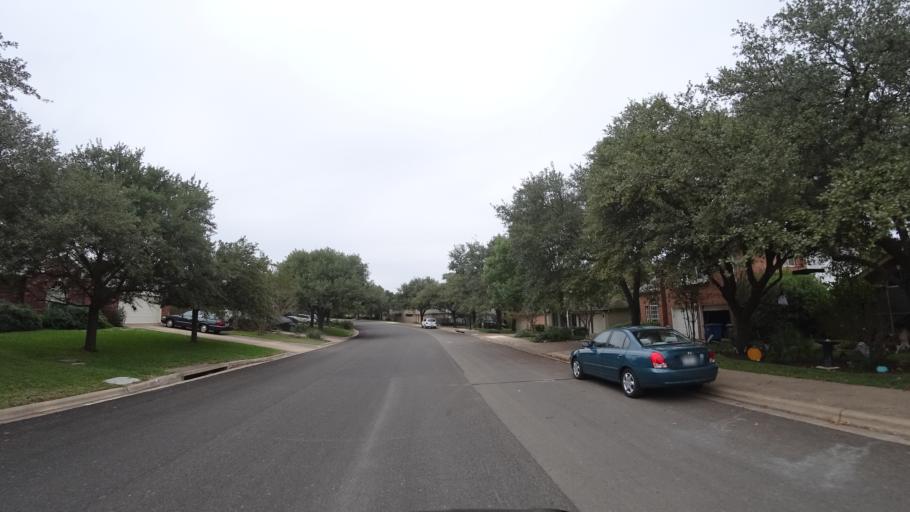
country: US
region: Texas
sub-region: Travis County
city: Shady Hollow
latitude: 30.1866
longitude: -97.8906
